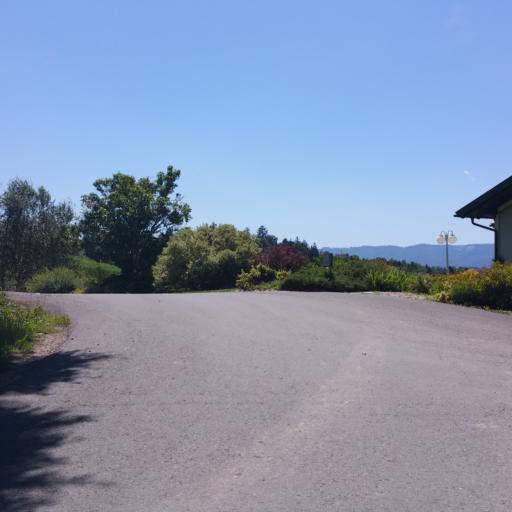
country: AT
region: Styria
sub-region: Politischer Bezirk Leibnitz
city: Gleinstatten
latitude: 46.7318
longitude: 15.3551
